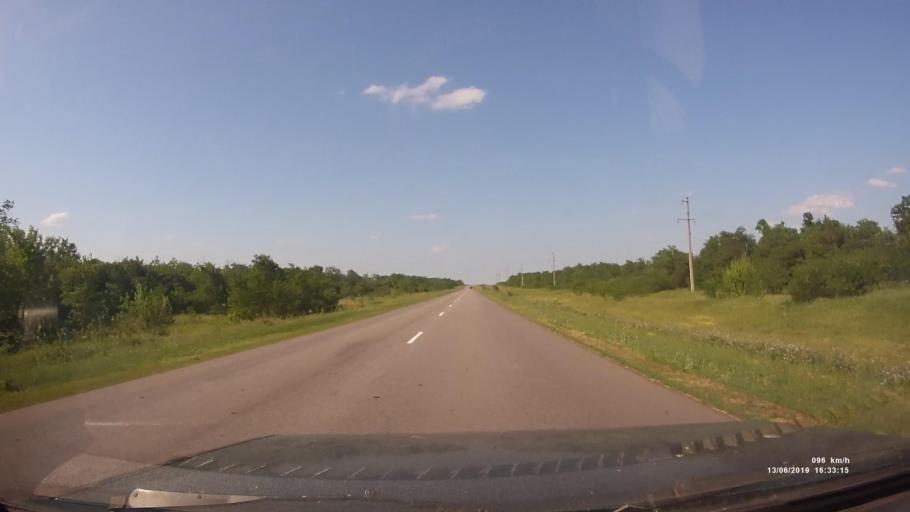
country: RU
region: Rostov
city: Kazanskaya
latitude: 49.8584
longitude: 41.2785
